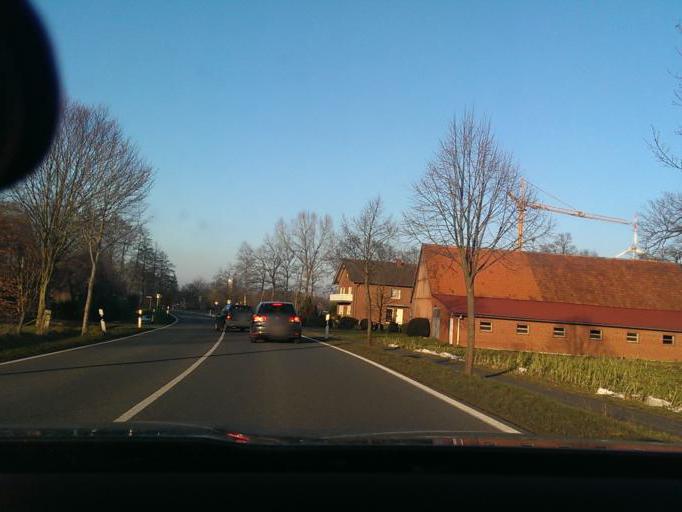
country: DE
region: North Rhine-Westphalia
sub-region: Regierungsbezirk Detmold
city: Hovelhof
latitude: 51.8107
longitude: 8.6194
